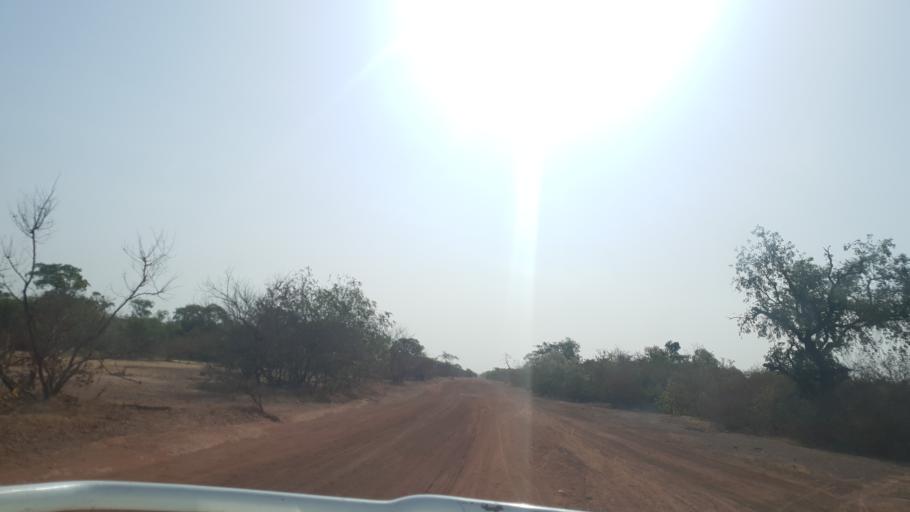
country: ML
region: Koulikoro
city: Dioila
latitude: 12.6918
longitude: -6.7495
